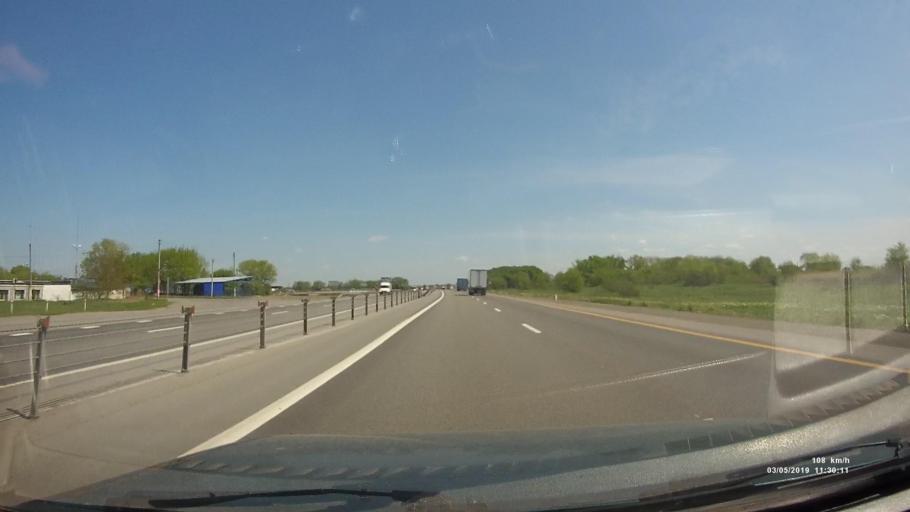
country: RU
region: Rostov
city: Bataysk
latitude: 47.0984
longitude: 39.8112
